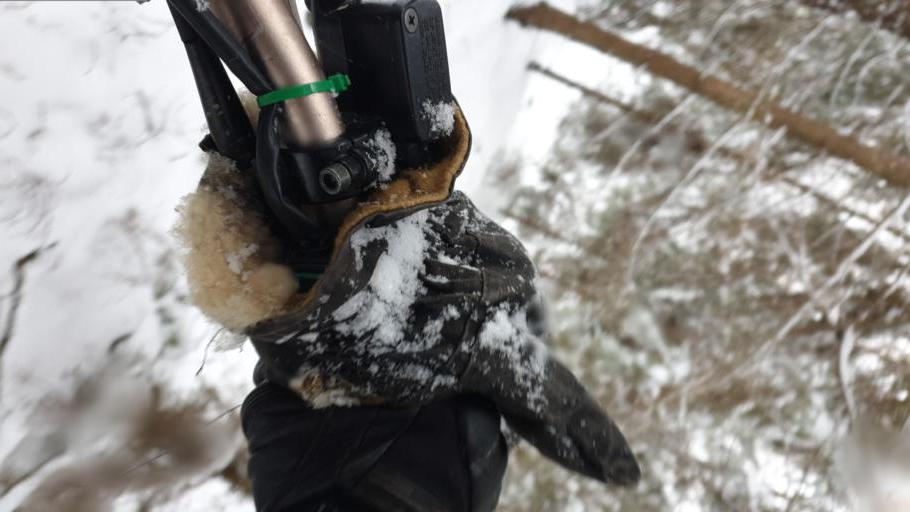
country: BY
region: Vitebsk
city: Lyepyel'
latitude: 54.9213
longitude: 28.5189
